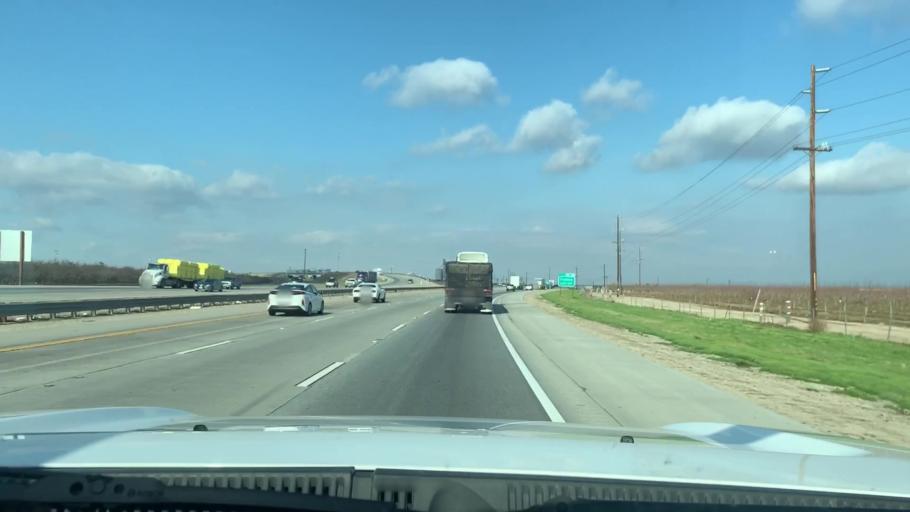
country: US
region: California
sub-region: Kern County
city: McFarland
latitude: 35.5847
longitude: -119.2041
